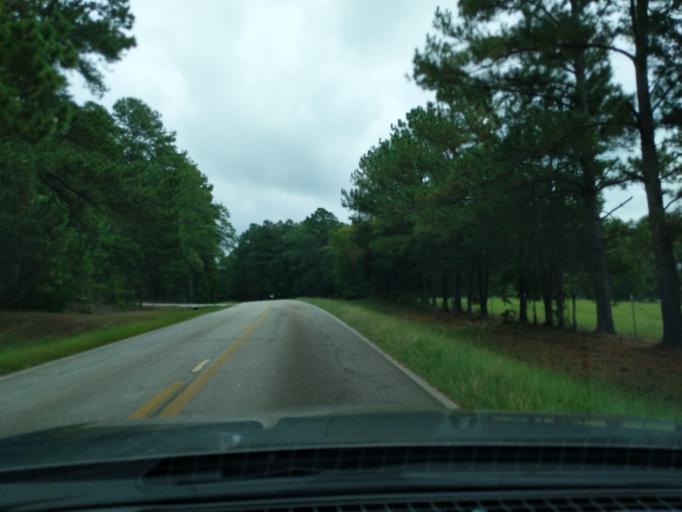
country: US
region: Georgia
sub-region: Columbia County
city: Appling
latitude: 33.5640
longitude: -82.3594
